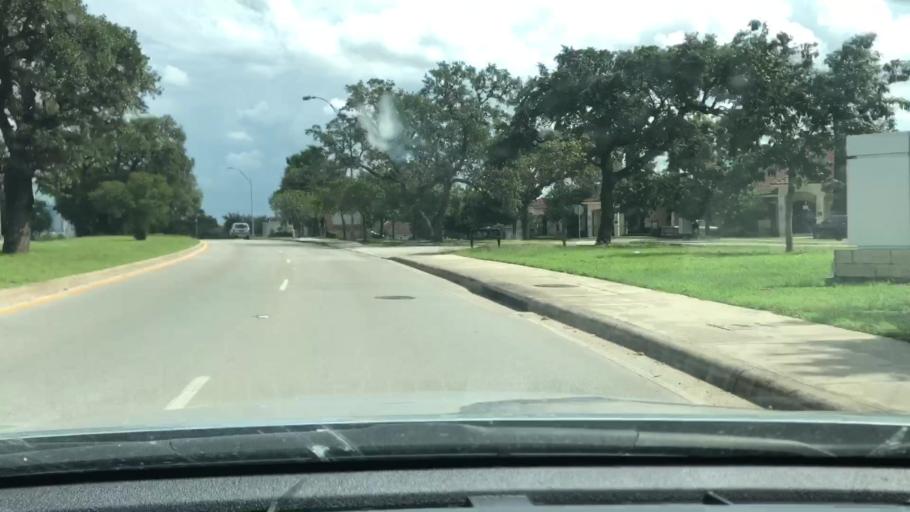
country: US
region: Texas
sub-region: Bexar County
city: Hollywood Park
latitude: 29.6143
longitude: -98.4767
